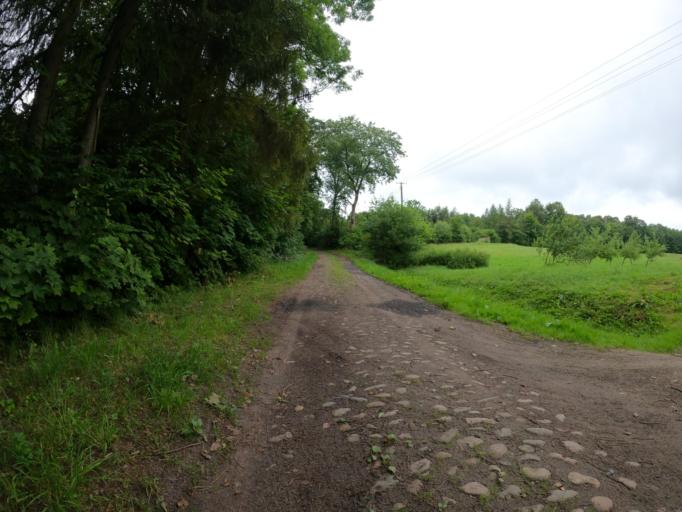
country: PL
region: West Pomeranian Voivodeship
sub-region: Powiat koszalinski
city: Bobolice
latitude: 53.9244
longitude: 16.4936
